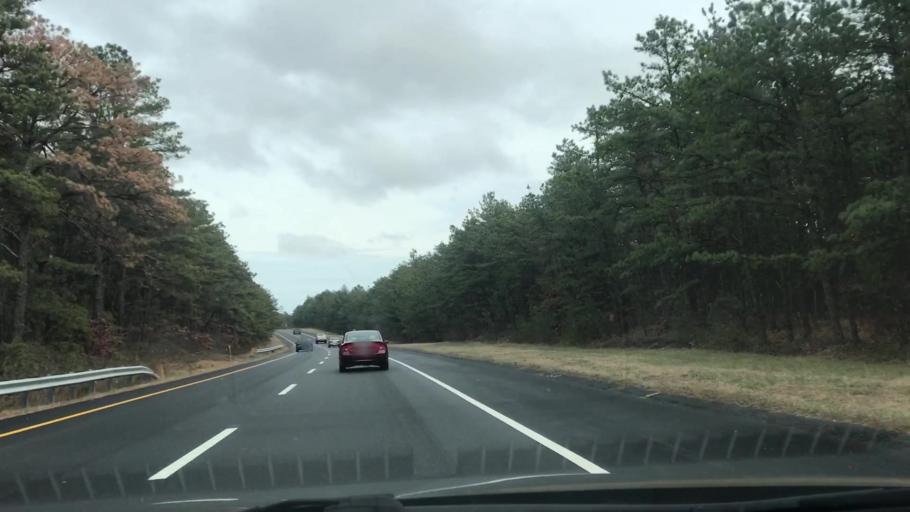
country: US
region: New York
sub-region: Suffolk County
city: Riverside
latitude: 40.9067
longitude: -72.7009
